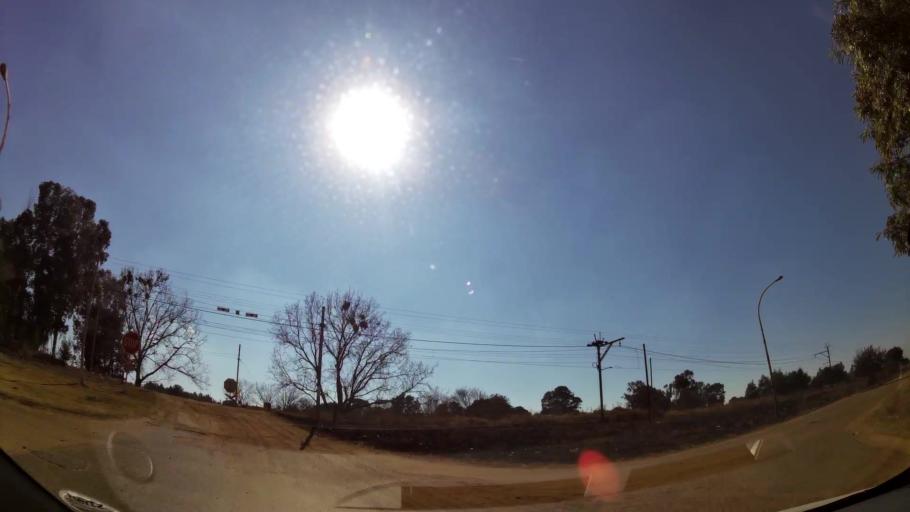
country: ZA
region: Mpumalanga
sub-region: Nkangala District Municipality
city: Witbank
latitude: -25.8267
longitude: 29.2490
